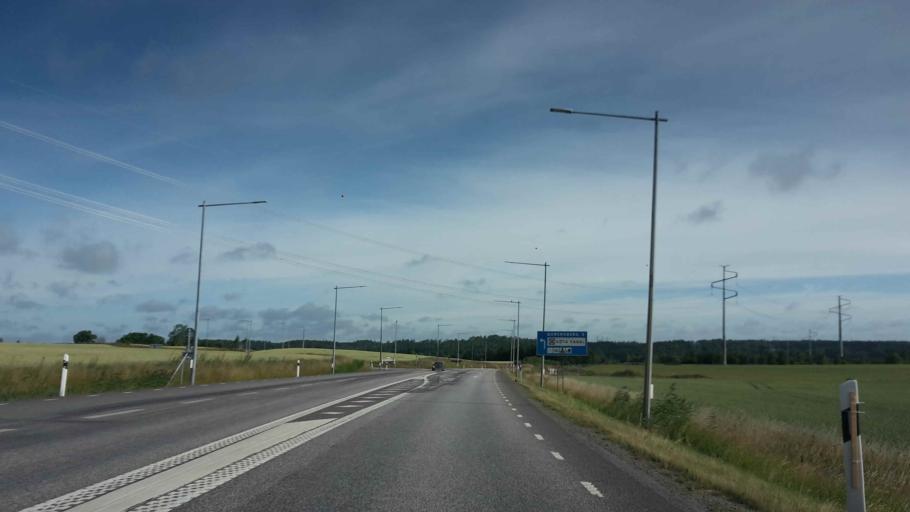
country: SE
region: OEstergoetland
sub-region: Motala Kommun
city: Borensberg
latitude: 58.5426
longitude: 15.3215
